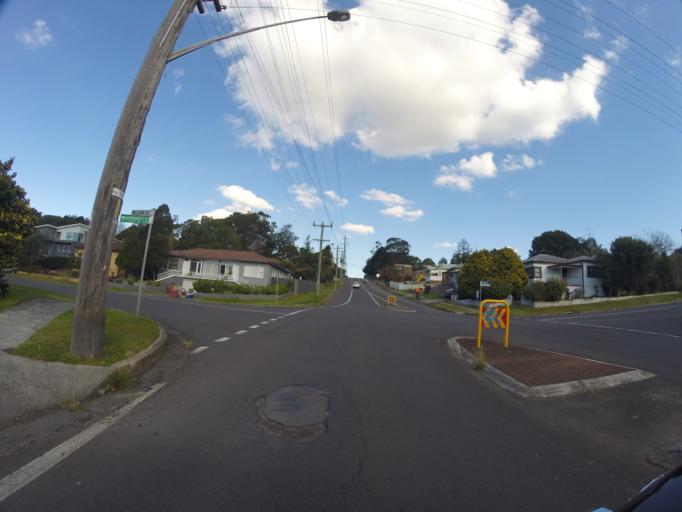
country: AU
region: New South Wales
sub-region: Wollongong
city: Keiraville
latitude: -34.4184
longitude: 150.8696
